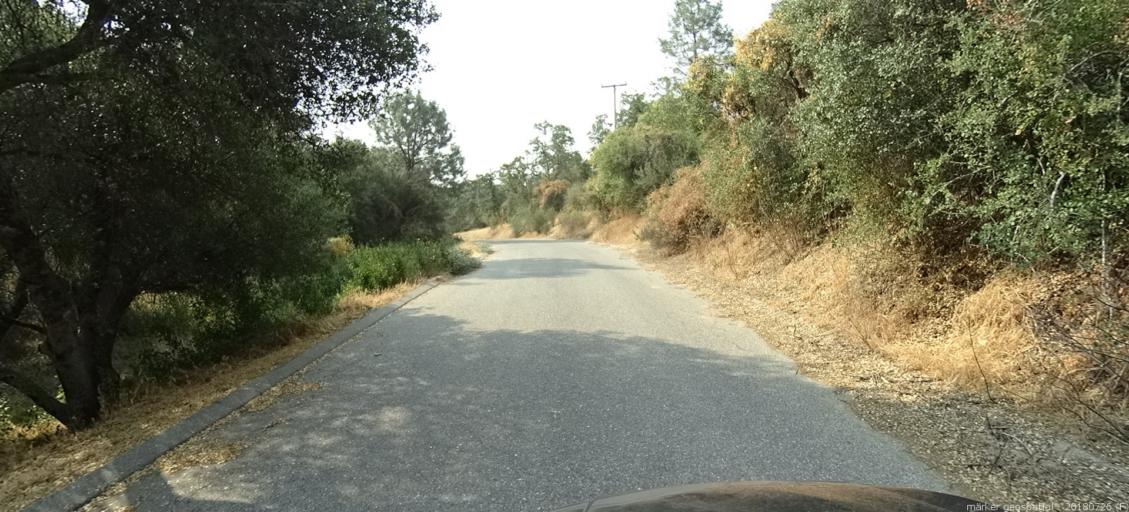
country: US
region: California
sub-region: Madera County
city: Coarsegold
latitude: 37.1934
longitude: -119.6829
